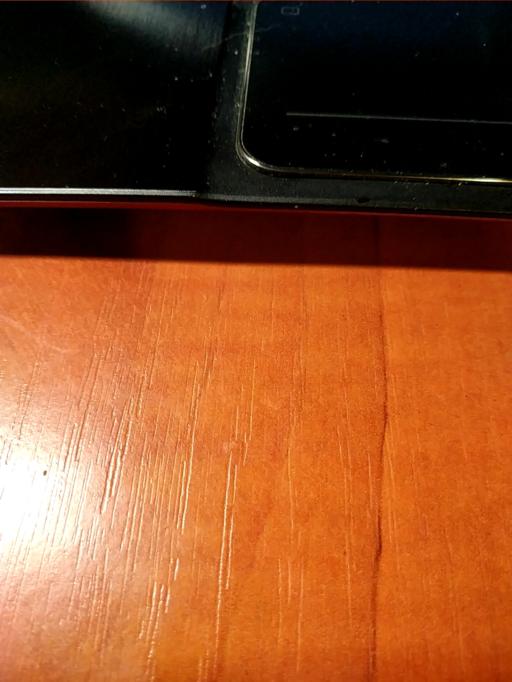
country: RU
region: Tverskaya
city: Ves'yegonsk
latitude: 58.7867
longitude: 37.5436
